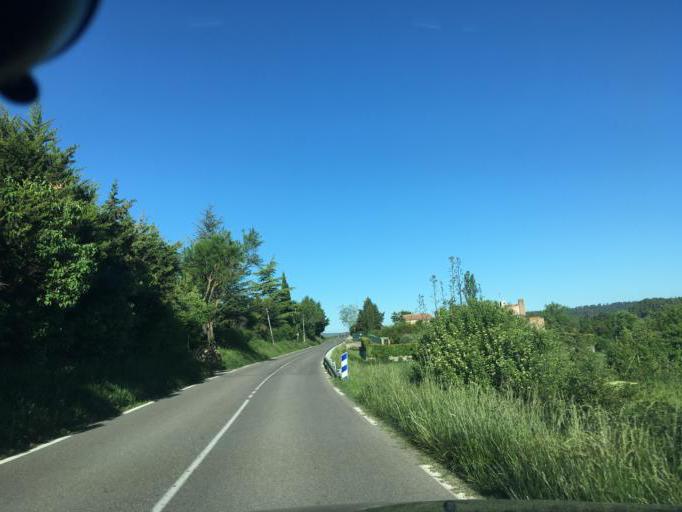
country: FR
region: Provence-Alpes-Cote d'Azur
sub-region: Departement du Var
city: Rians
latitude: 43.6120
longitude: 5.7298
